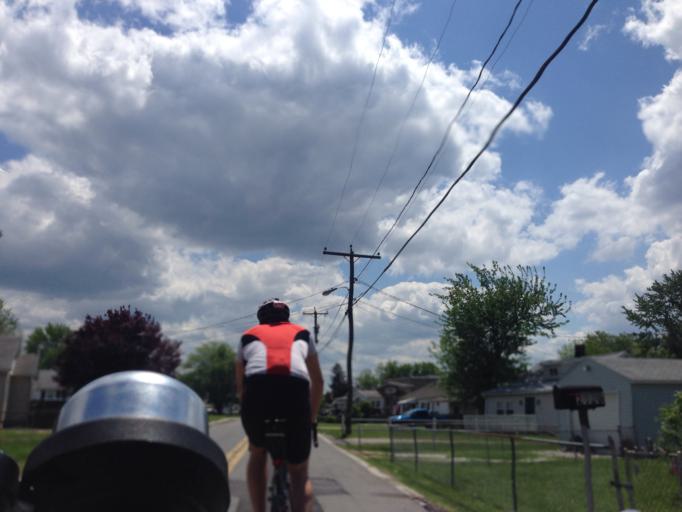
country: US
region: Maryland
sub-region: Baltimore County
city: Edgemere
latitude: 39.2222
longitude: -76.4523
